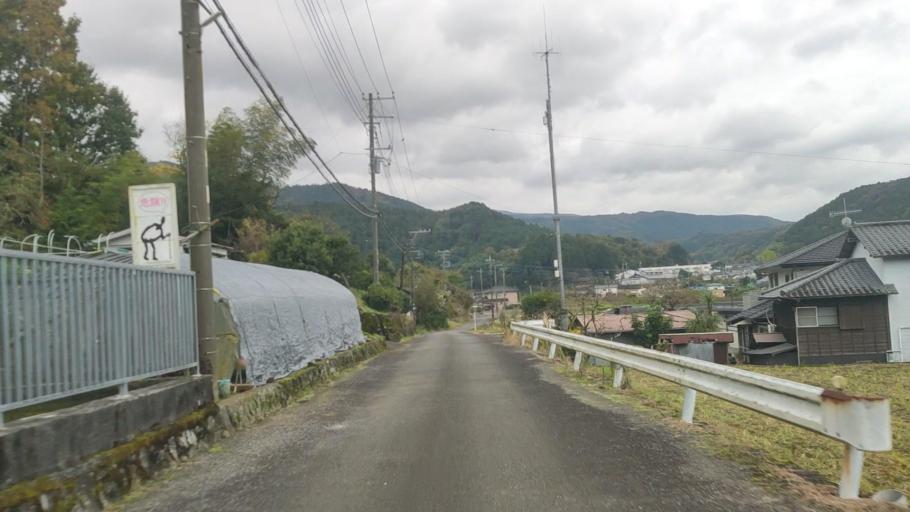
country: JP
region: Shizuoka
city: Ito
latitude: 34.9292
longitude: 139.0038
